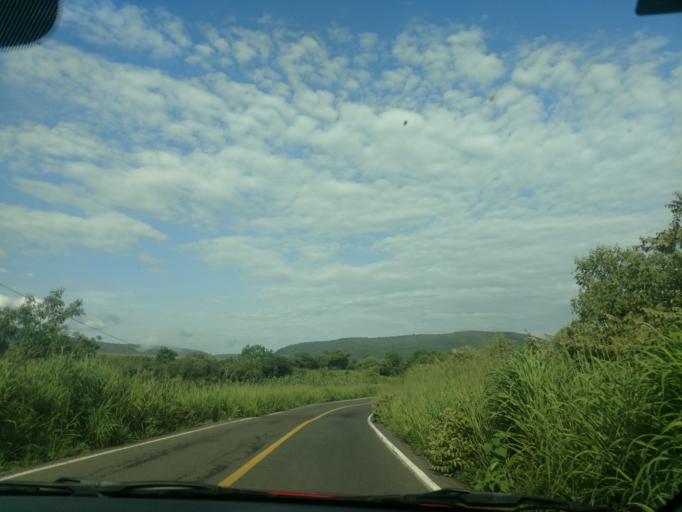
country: MX
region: Jalisco
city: Ameca
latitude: 20.5199
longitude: -104.1186
